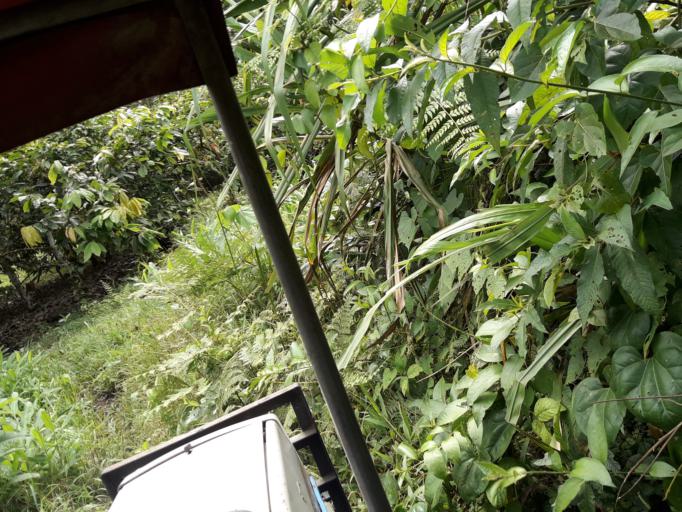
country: EC
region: Napo
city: Tena
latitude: -1.0694
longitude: -77.7952
